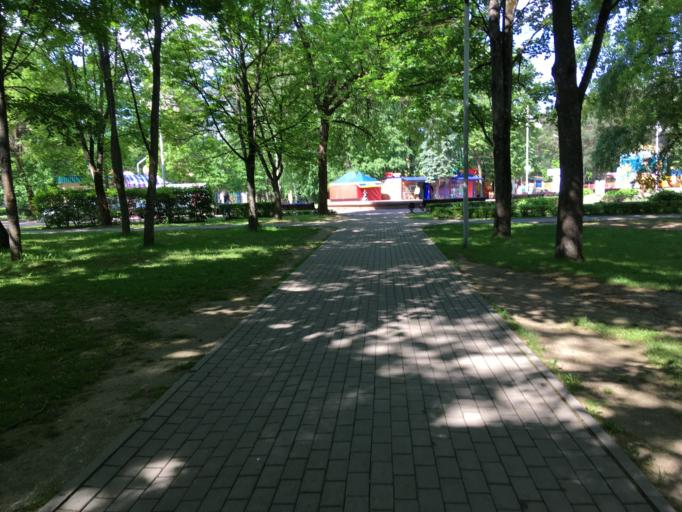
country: BY
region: Minsk
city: Minsk
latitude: 53.9197
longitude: 27.6158
